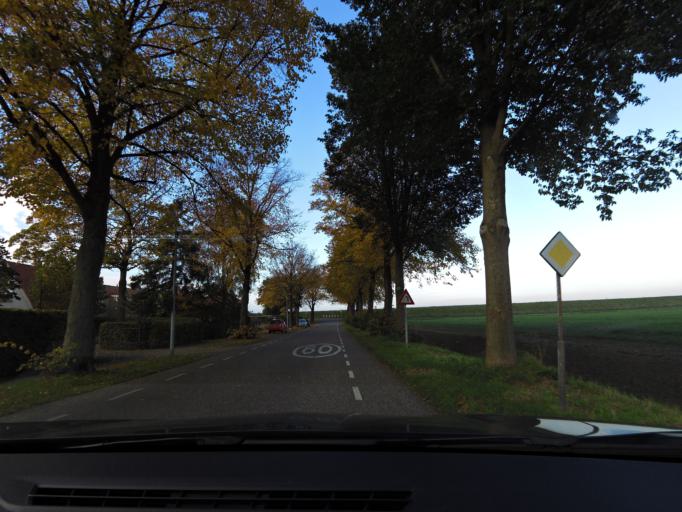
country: NL
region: North Brabant
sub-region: Gemeente Steenbergen
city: Dinteloord
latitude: 51.7160
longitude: 4.2892
